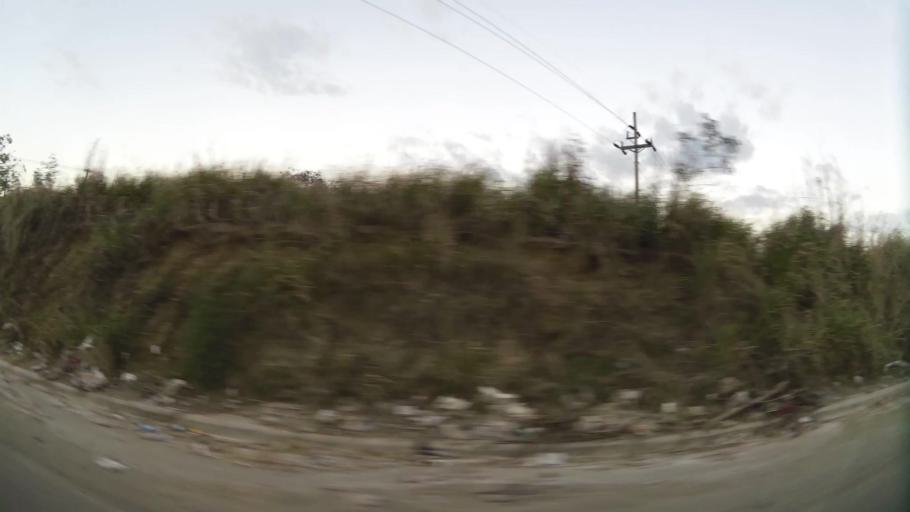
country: DO
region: Nacional
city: La Agustina
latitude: 18.5534
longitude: -69.9454
